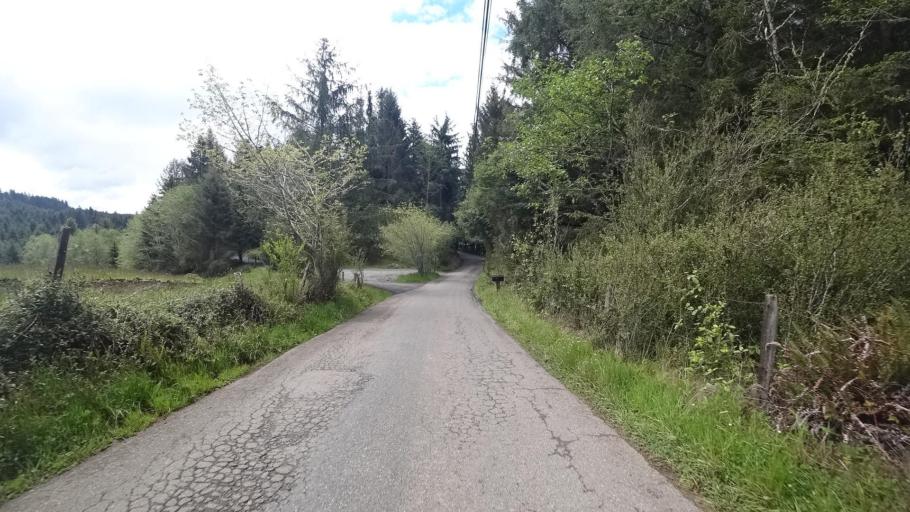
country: US
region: California
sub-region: Humboldt County
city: Bayside
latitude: 40.8383
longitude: -124.0234
